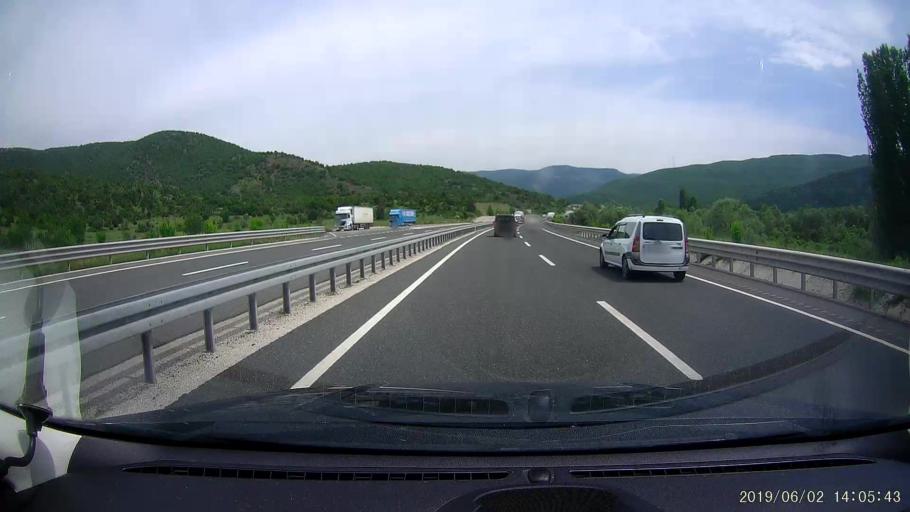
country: TR
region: Cankiri
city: Ilgaz
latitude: 40.8982
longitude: 33.6735
